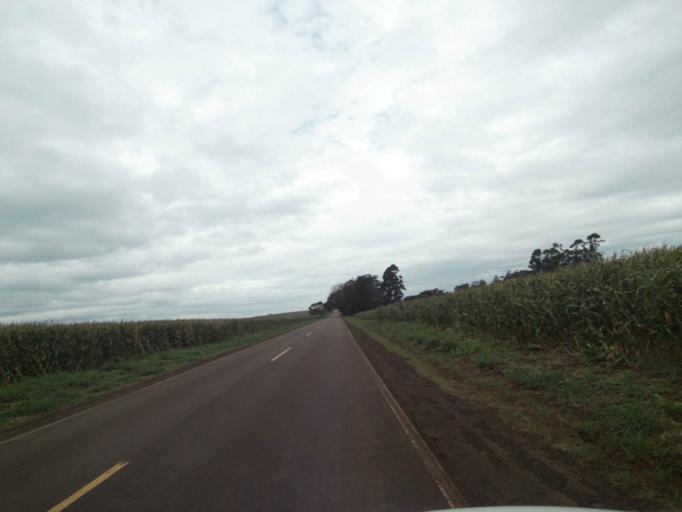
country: BR
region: Parana
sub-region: Marechal Candido Rondon
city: Marechal Candido Rondon
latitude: -24.8192
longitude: -54.1811
